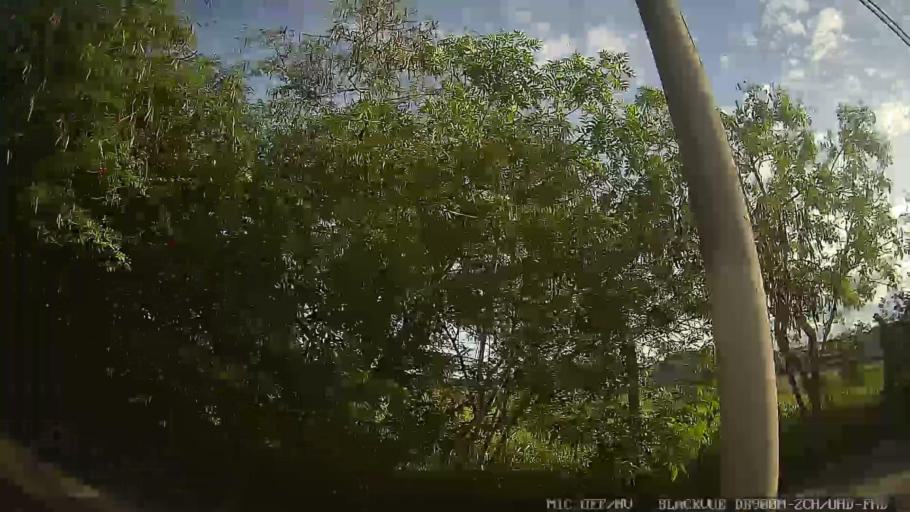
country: BR
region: Sao Paulo
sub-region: Mogi das Cruzes
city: Mogi das Cruzes
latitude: -23.5125
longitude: -46.1597
